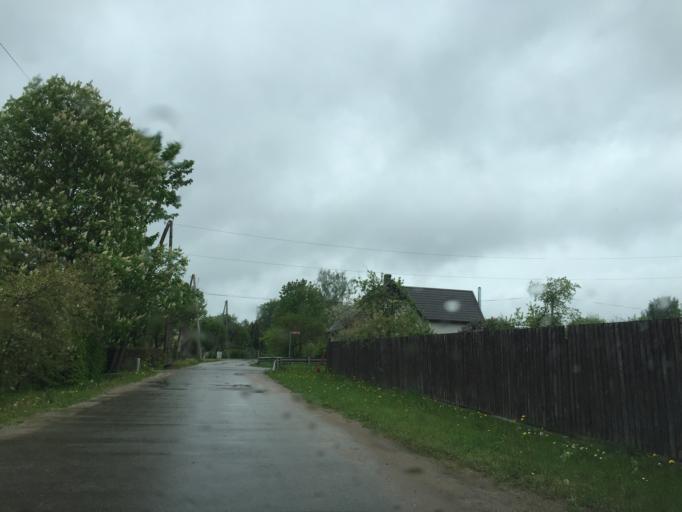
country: LV
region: Lielvarde
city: Lielvarde
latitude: 56.7215
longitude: 24.7940
